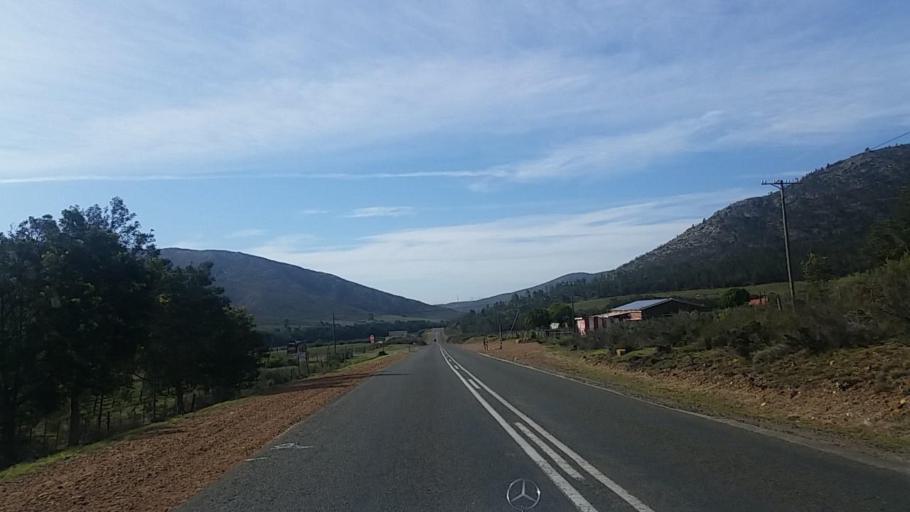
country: ZA
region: Western Cape
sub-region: Eden District Municipality
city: George
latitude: -33.8428
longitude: 22.3502
